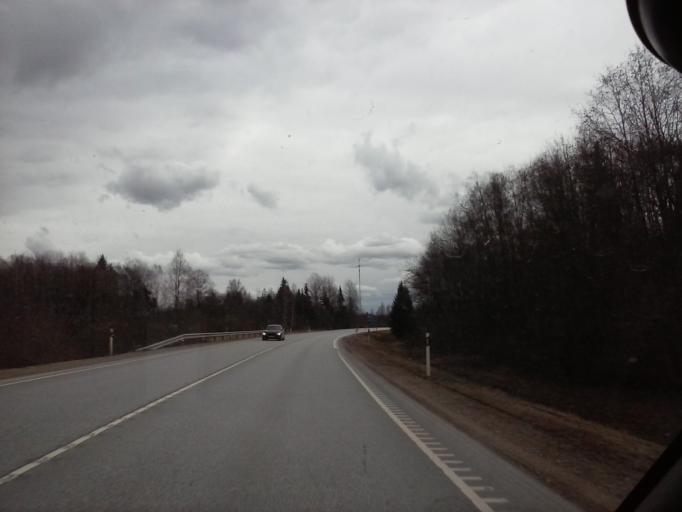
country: EE
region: Harju
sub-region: Anija vald
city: Kehra
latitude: 59.1647
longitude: 25.2795
